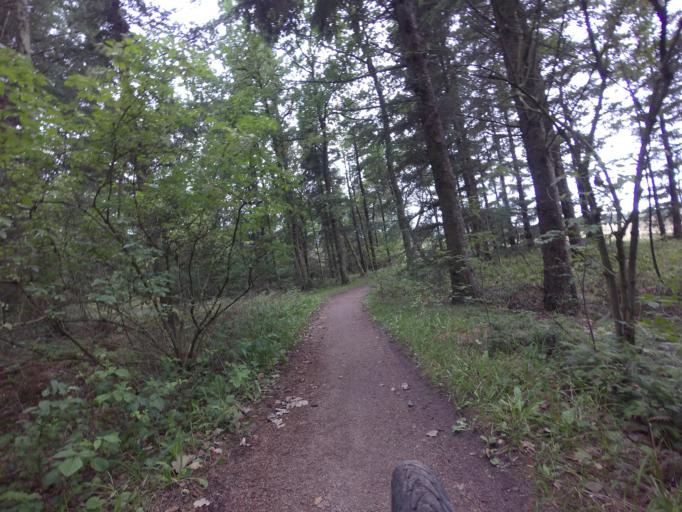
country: DK
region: North Denmark
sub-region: Hjorring Kommune
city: Sindal
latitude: 57.5854
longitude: 10.1791
